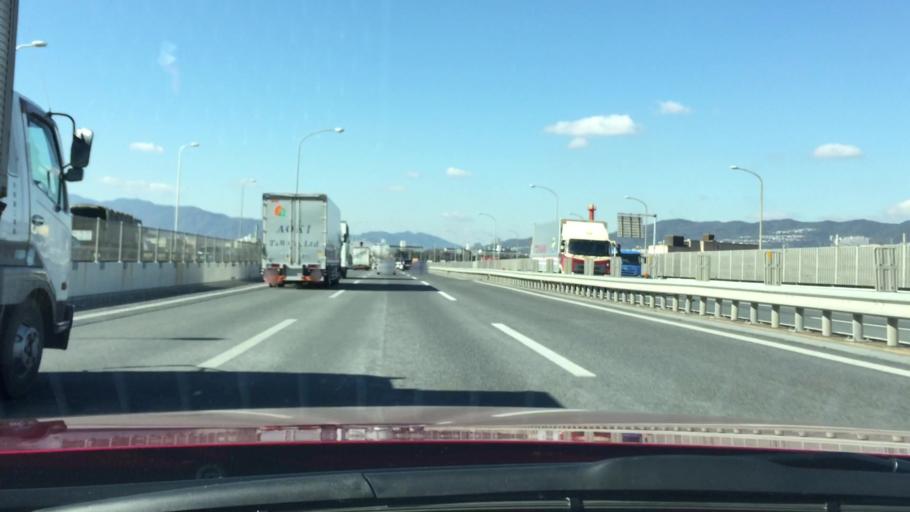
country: JP
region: Hyogo
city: Kawanishi
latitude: 34.8106
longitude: 135.4195
